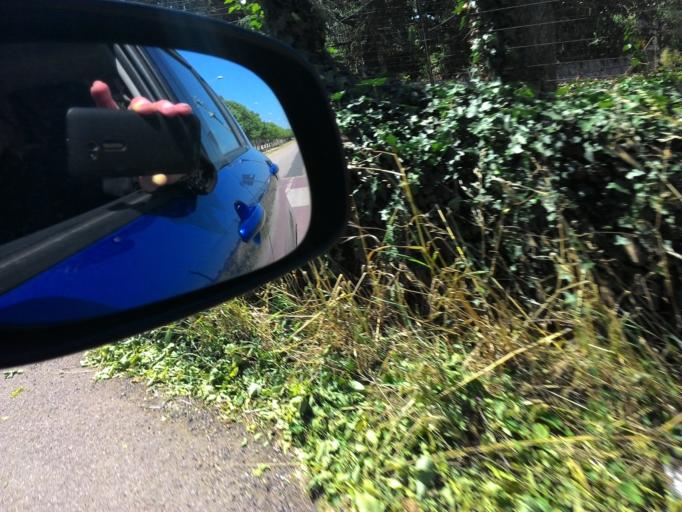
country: IT
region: Apulia
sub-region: Provincia di Bari
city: Putignano
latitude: 40.8475
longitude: 17.1459
